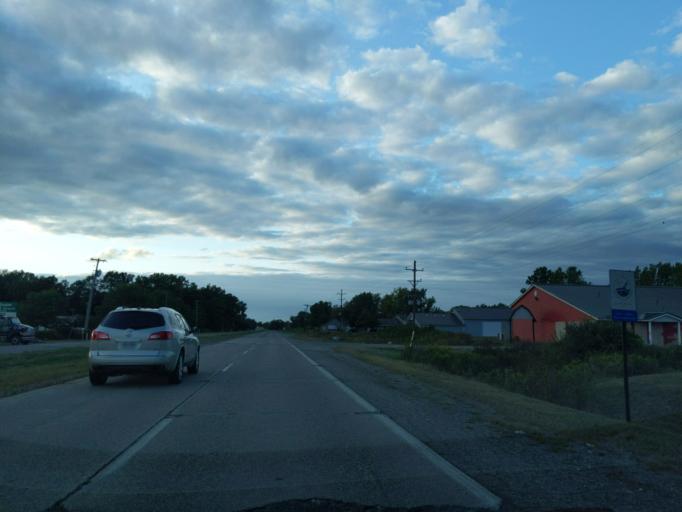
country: US
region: Michigan
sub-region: Ingham County
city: Holt
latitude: 42.6199
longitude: -84.4990
